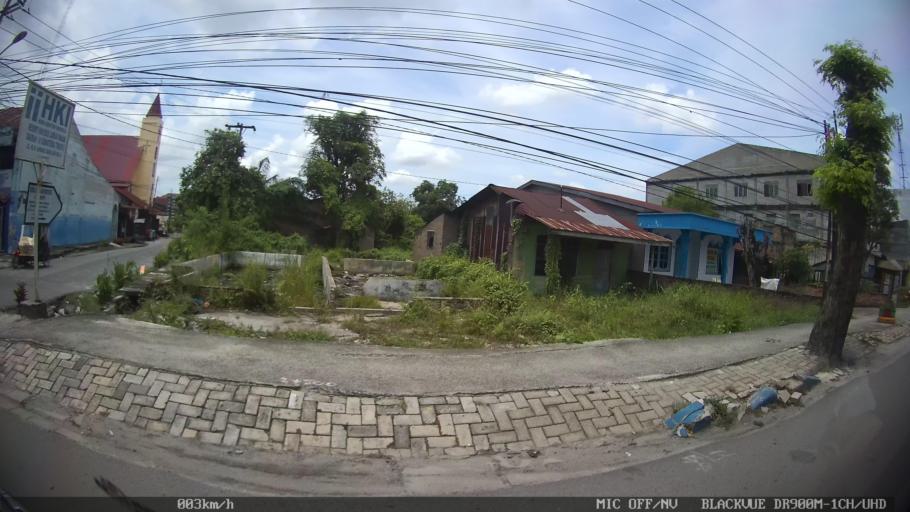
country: ID
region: North Sumatra
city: Percut
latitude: 3.5544
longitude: 98.8761
